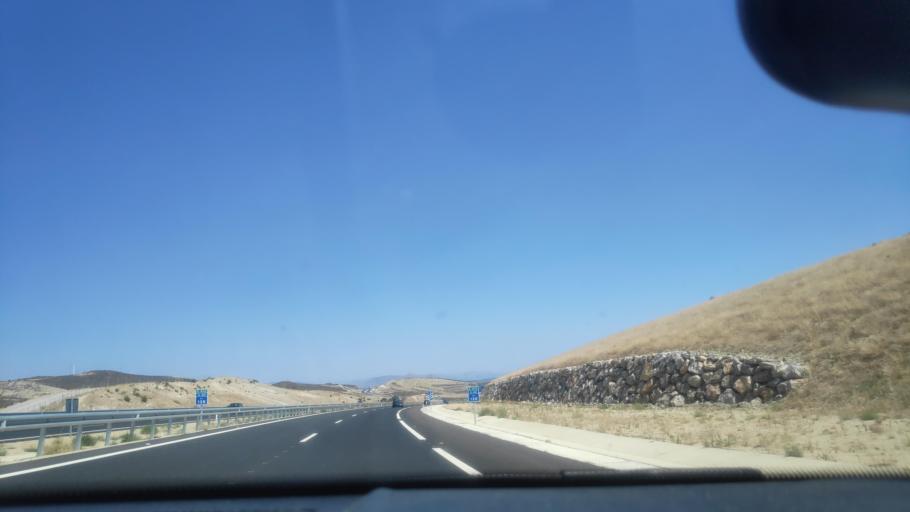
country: ES
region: Andalusia
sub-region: Provincia de Granada
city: Alhendin
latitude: 37.0940
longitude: -3.6733
